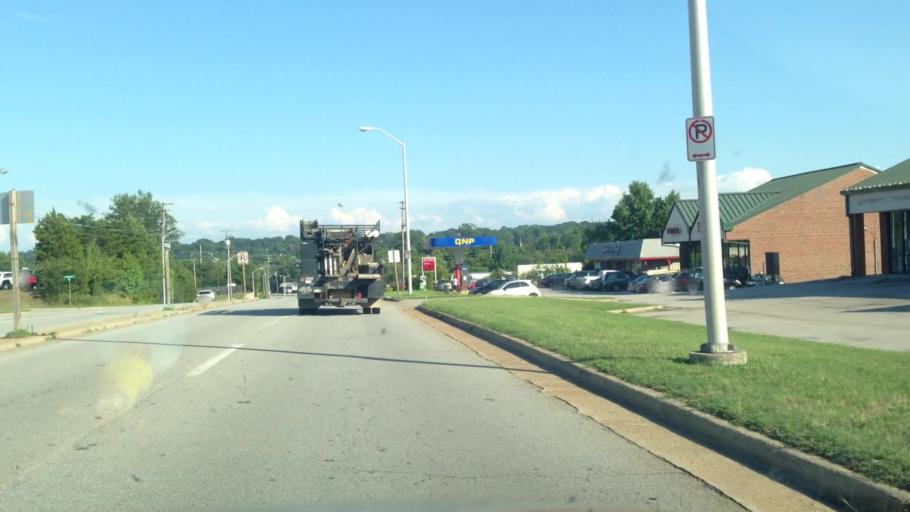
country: US
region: Virginia
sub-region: City of Danville
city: Danville
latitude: 36.5934
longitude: -79.4270
